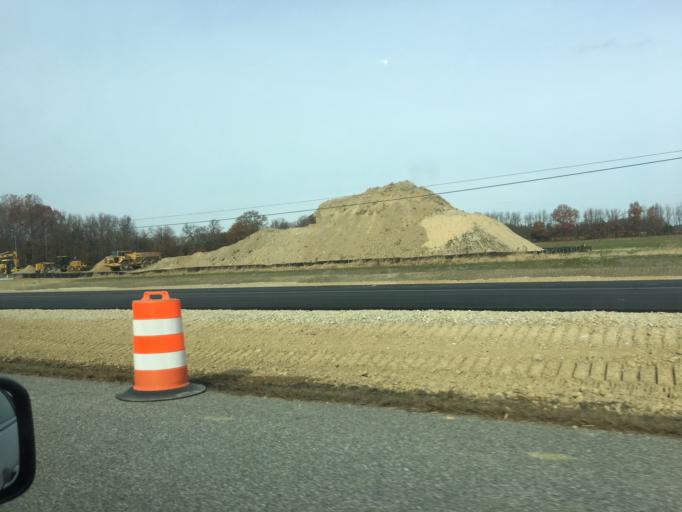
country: US
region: Maryland
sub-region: Queen Anne's County
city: Centreville
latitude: 38.9316
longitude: -76.0203
